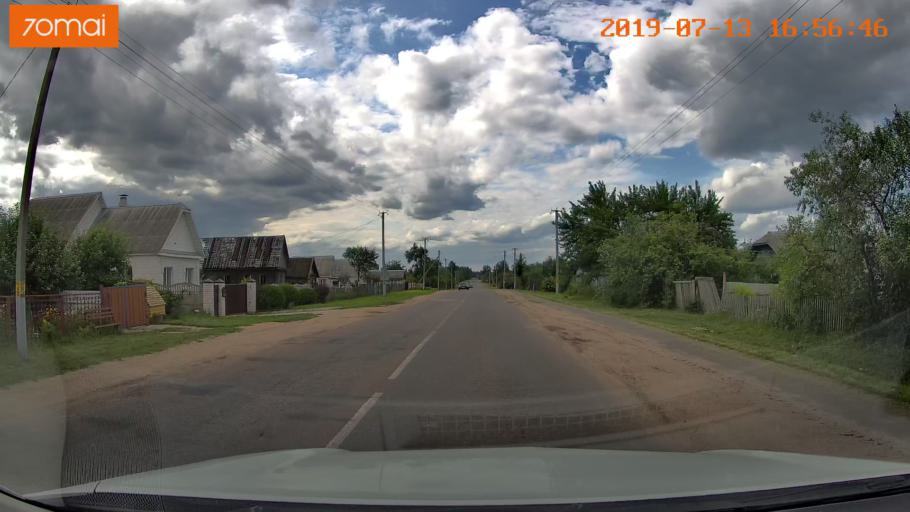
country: BY
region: Mogilev
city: Kirawsk
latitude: 53.2752
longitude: 29.4571
